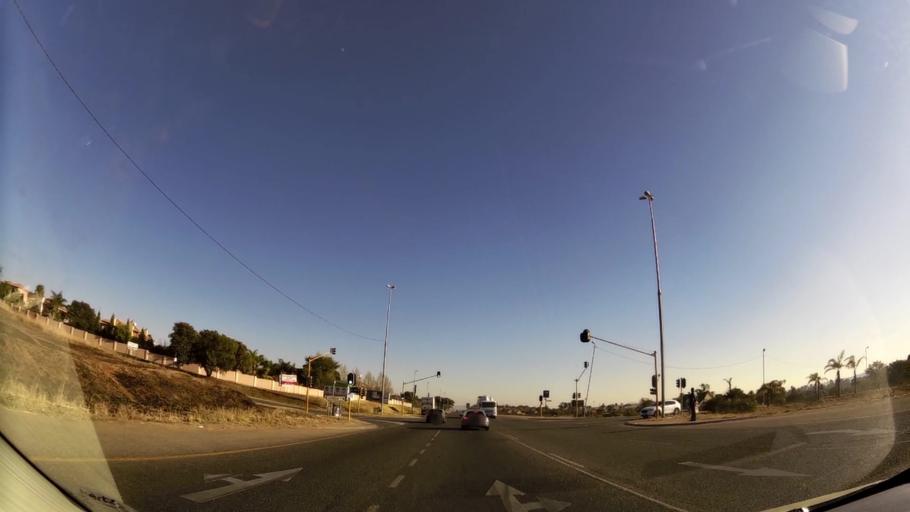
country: ZA
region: Gauteng
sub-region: West Rand District Municipality
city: Muldersdriseloop
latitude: -26.0802
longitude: 27.8595
